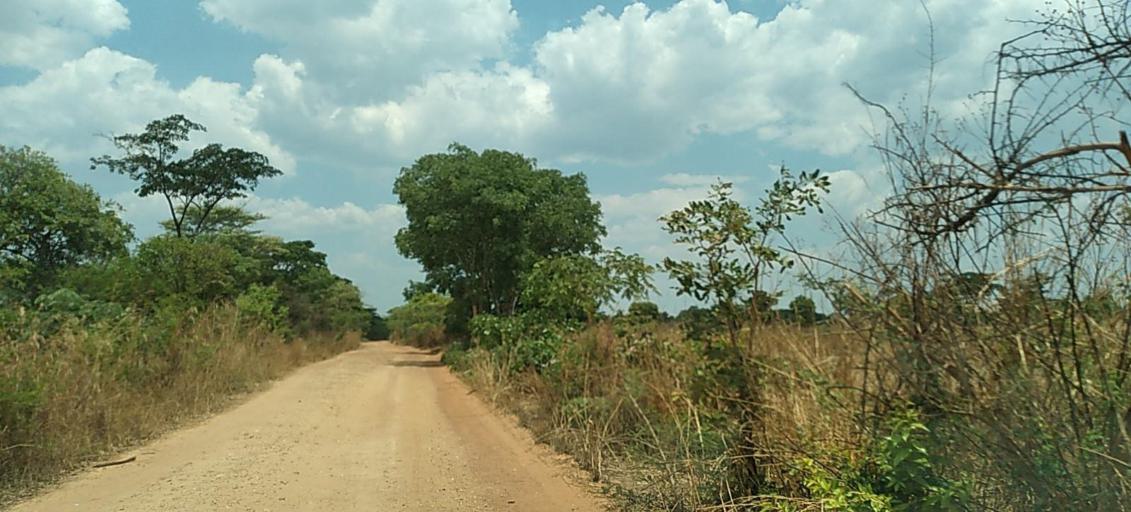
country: ZM
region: Copperbelt
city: Luanshya
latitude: -13.3770
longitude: 28.4294
